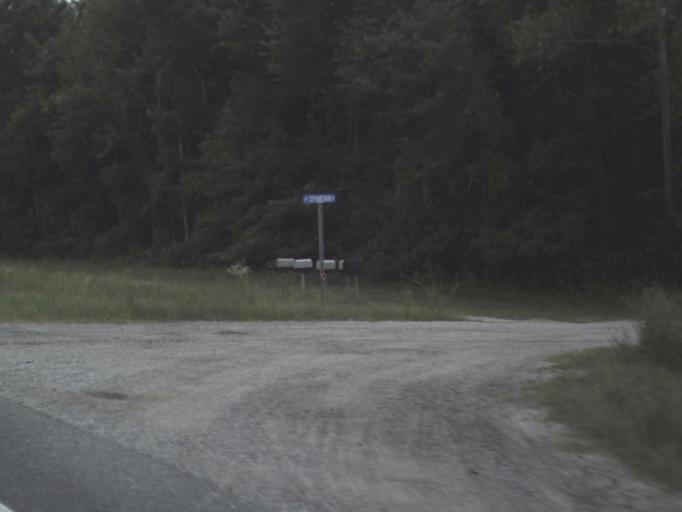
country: US
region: Florida
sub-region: Columbia County
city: Lake City
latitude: 30.1254
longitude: -82.6223
